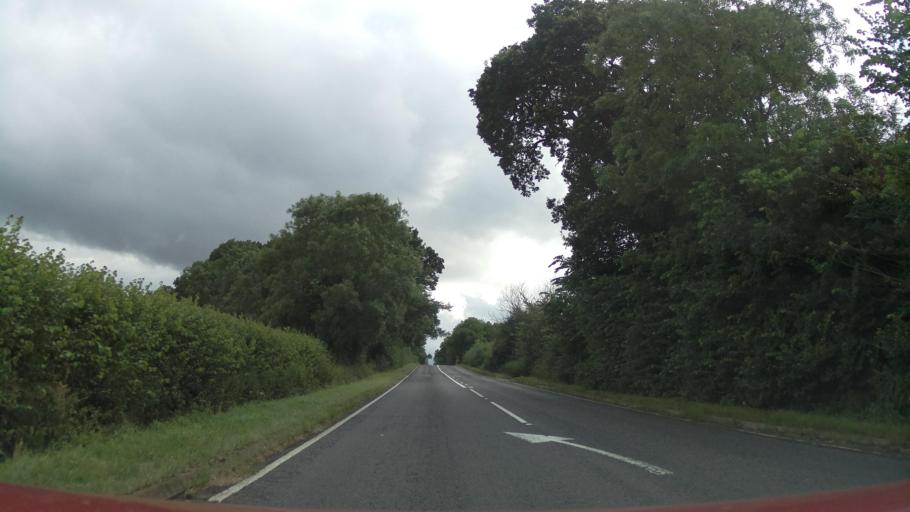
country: GB
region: England
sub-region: Warwickshire
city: Long Itchington
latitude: 52.2938
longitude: -1.3453
